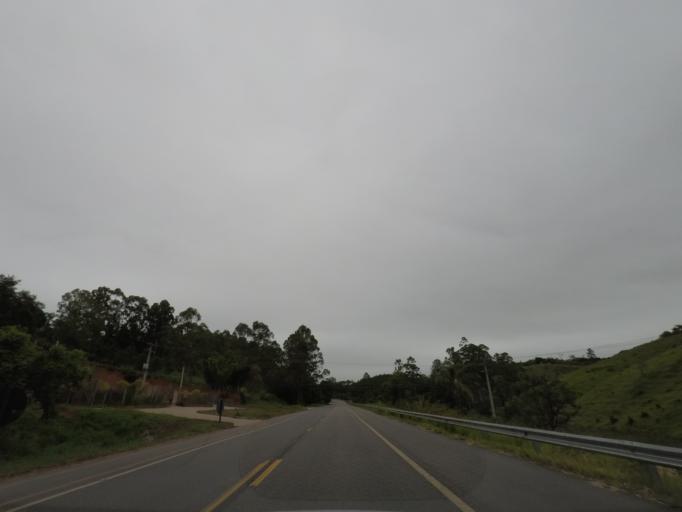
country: BR
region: Sao Paulo
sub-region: Cunha
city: Cunha
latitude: -23.0672
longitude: -44.9669
